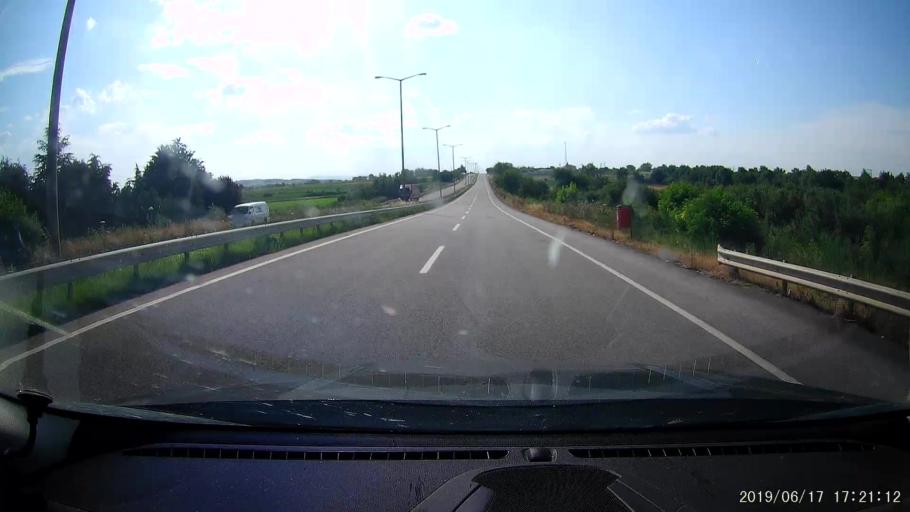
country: GR
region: East Macedonia and Thrace
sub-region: Nomos Evrou
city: Rizia
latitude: 41.7048
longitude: 26.3990
